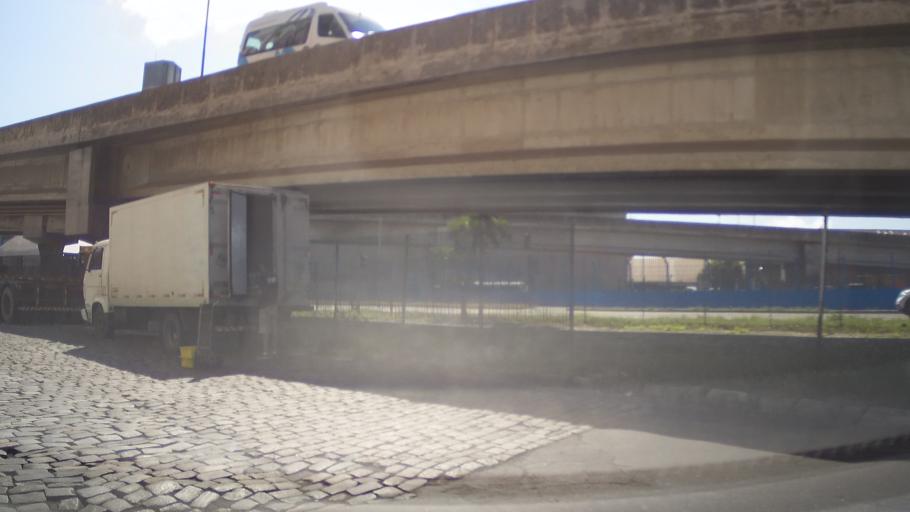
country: BR
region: Sao Paulo
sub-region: Santos
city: Santos
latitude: -23.9383
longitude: -46.3160
